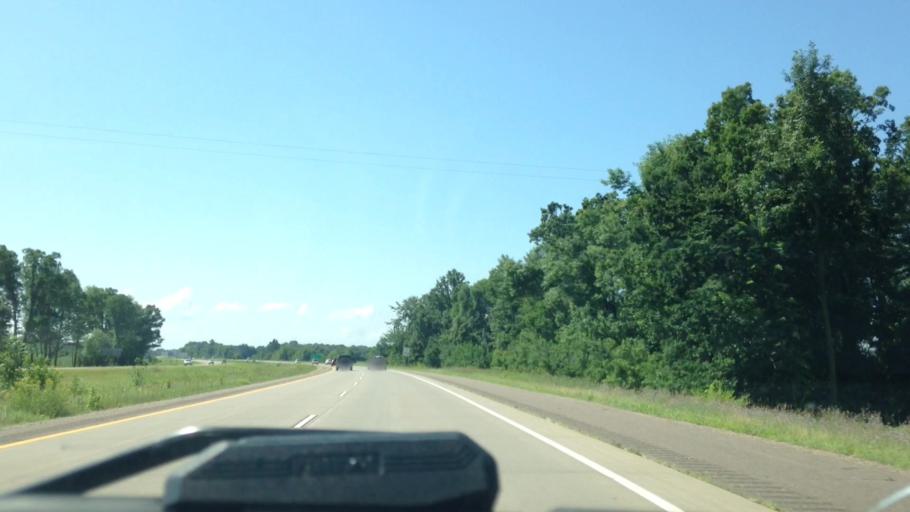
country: US
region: Wisconsin
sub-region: Barron County
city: Rice Lake
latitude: 45.4594
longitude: -91.7596
